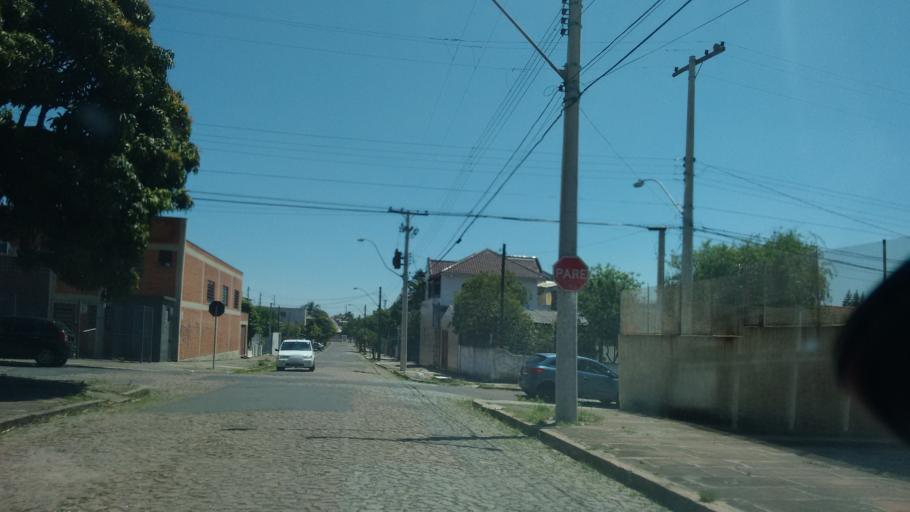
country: BR
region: Rio Grande do Sul
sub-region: Cachoeirinha
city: Cachoeirinha
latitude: -29.9993
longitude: -51.1288
